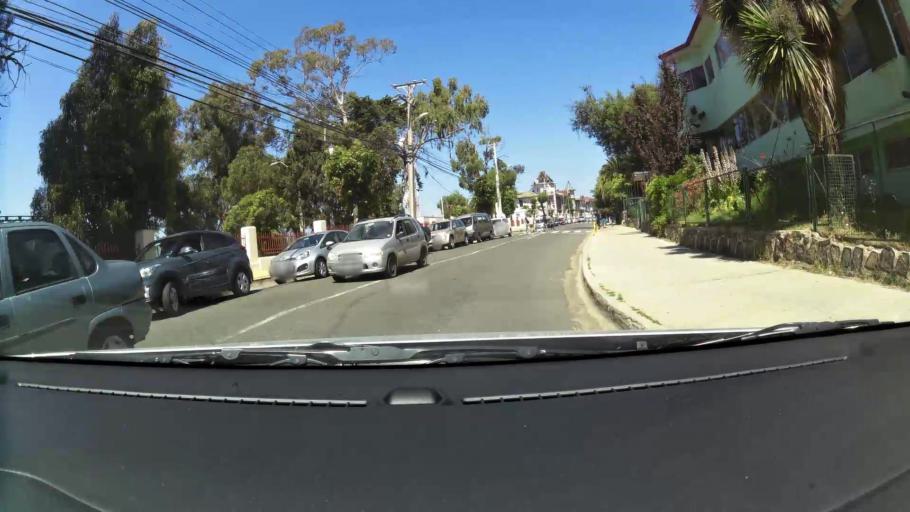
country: CL
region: Valparaiso
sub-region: Provincia de Valparaiso
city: Valparaiso
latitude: -33.0266
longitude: -71.6358
